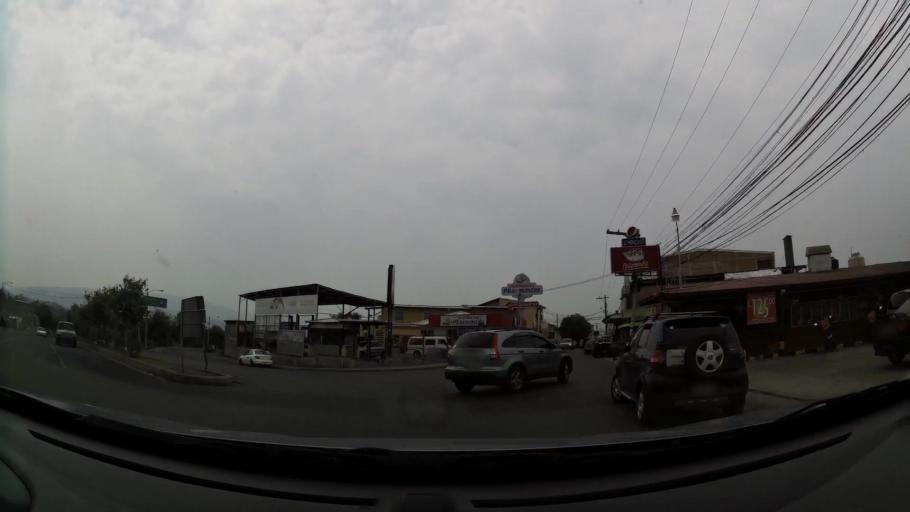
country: HN
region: Francisco Morazan
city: Yaguacire
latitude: 14.0427
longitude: -87.2228
